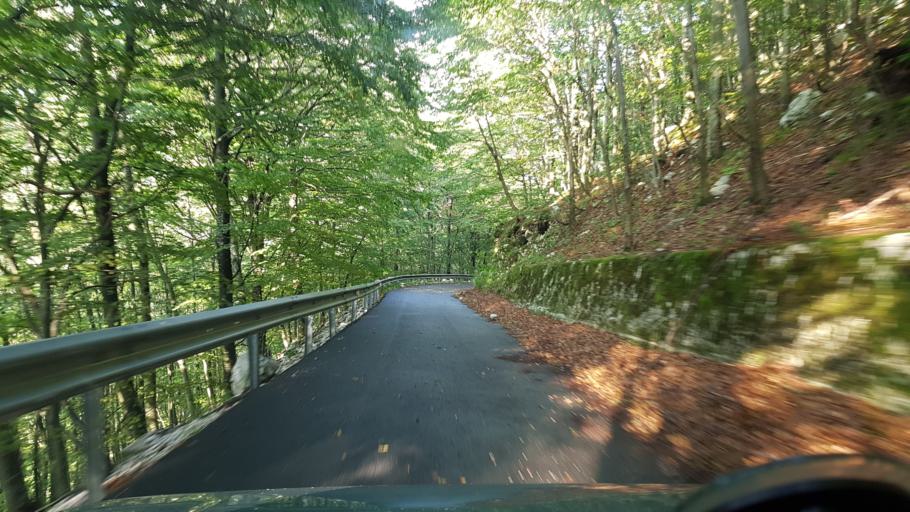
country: IT
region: Friuli Venezia Giulia
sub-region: Provincia di Udine
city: Lusevera
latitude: 46.3097
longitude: 13.2612
